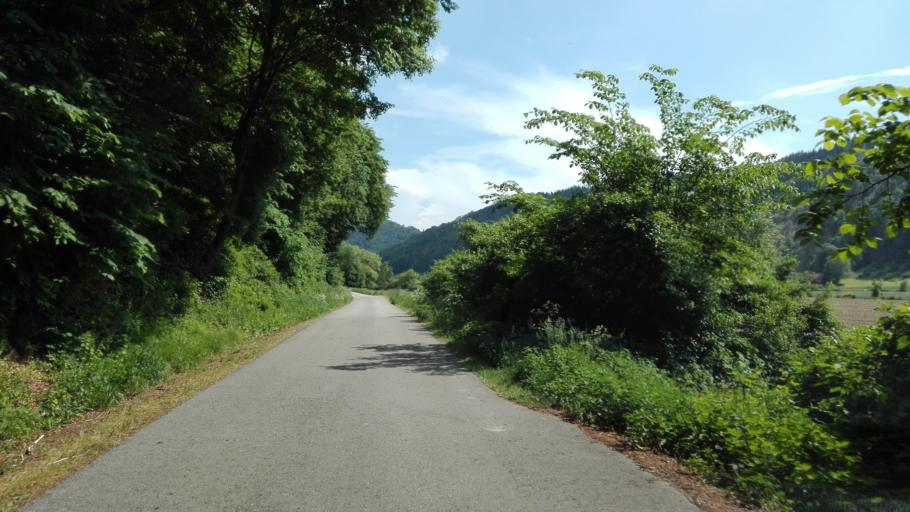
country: AT
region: Upper Austria
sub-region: Politischer Bezirk Rohrbach
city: Pfarrkirchen im Muehlkreis
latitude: 48.4407
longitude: 13.8603
